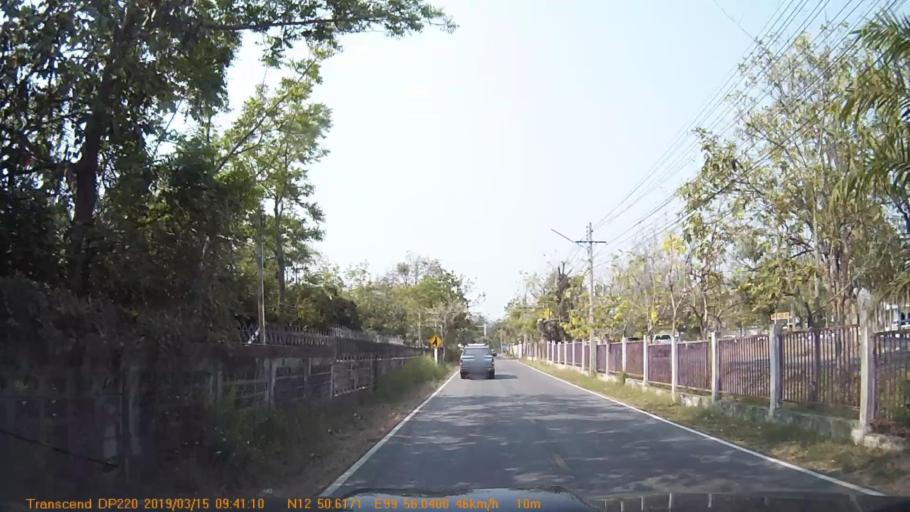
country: TH
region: Phetchaburi
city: Cha-am
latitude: 12.8436
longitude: 99.9341
